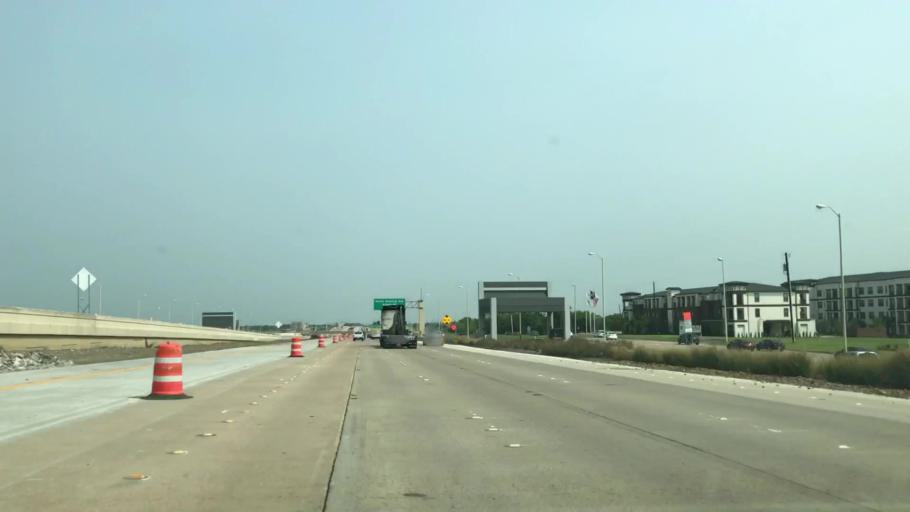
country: US
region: Texas
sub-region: Collin County
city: Murphy
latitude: 32.9741
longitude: -96.6554
